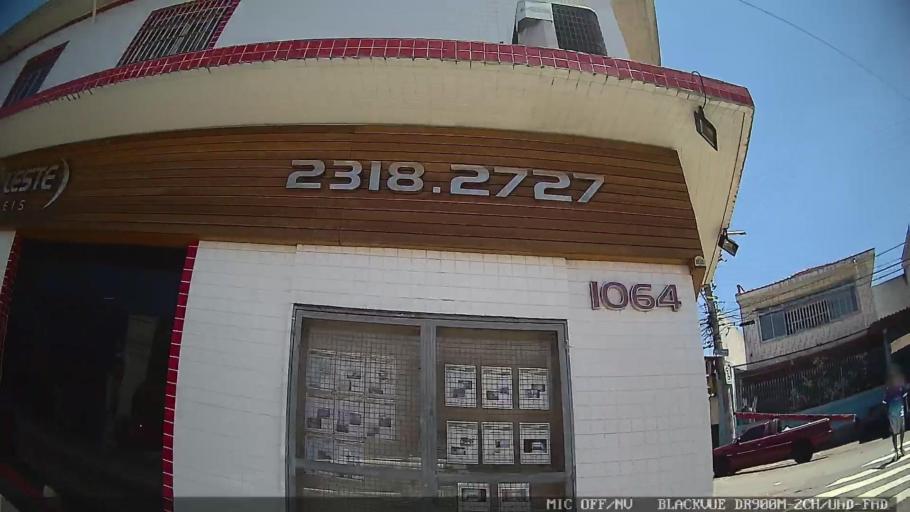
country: BR
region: Sao Paulo
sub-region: Sao Caetano Do Sul
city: Sao Caetano do Sul
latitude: -23.5963
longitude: -46.5561
